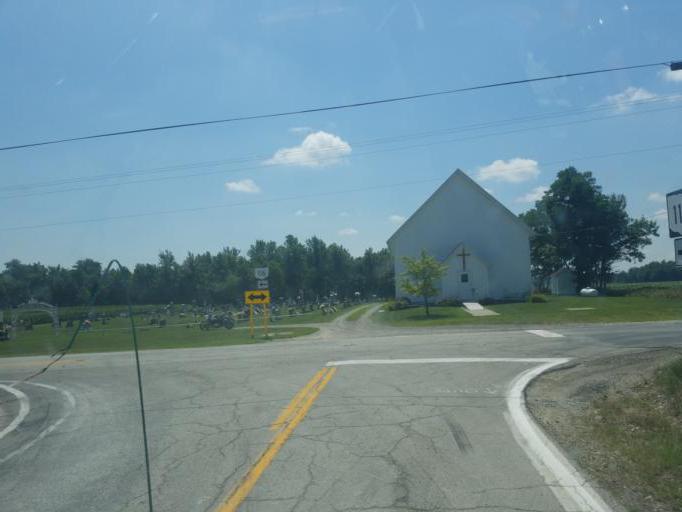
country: US
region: Ohio
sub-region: Allen County
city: Spencerville
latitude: 40.6771
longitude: -84.4255
